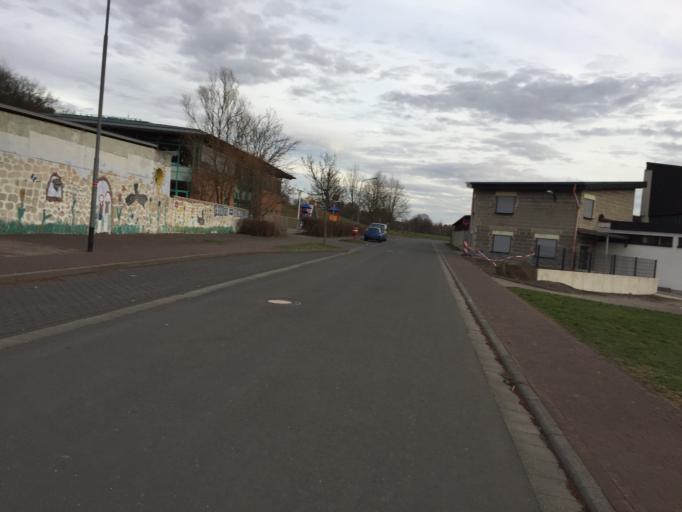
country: DE
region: Hesse
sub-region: Regierungsbezirk Giessen
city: Rabenau
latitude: 50.6757
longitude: 8.8704
